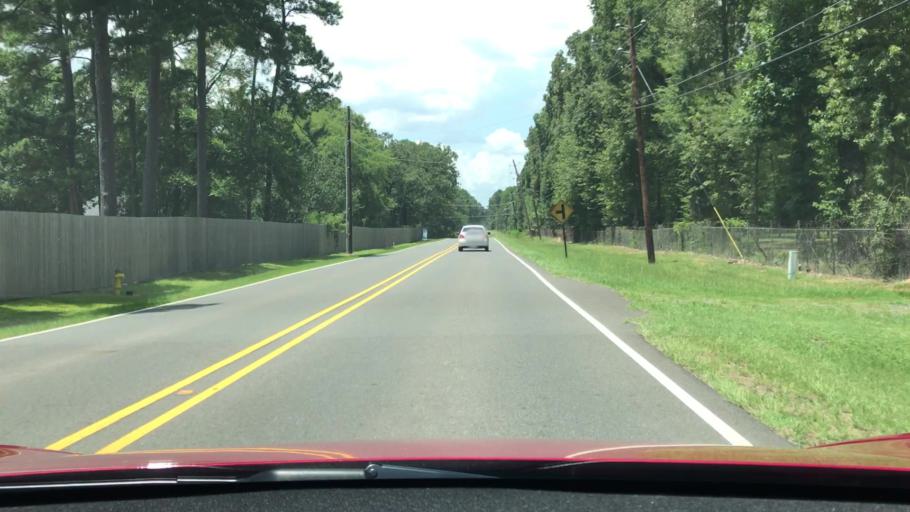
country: US
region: Louisiana
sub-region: Bossier Parish
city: Bossier City
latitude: 32.3665
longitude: -93.6946
